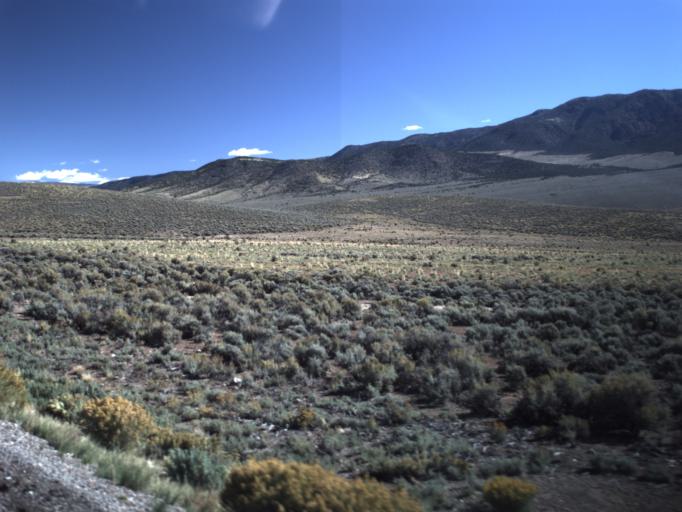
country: US
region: Utah
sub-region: Piute County
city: Junction
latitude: 38.3096
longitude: -111.9682
